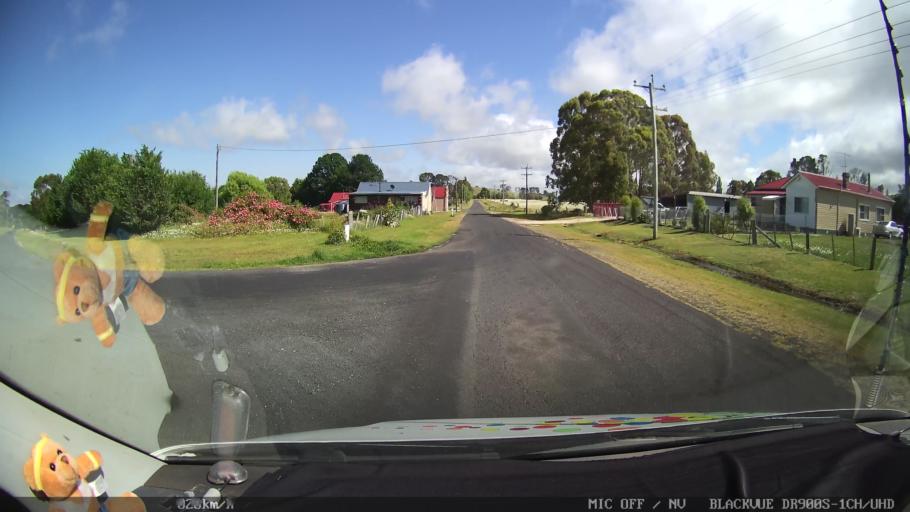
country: AU
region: New South Wales
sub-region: Guyra
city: Guyra
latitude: -30.0205
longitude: 151.6591
